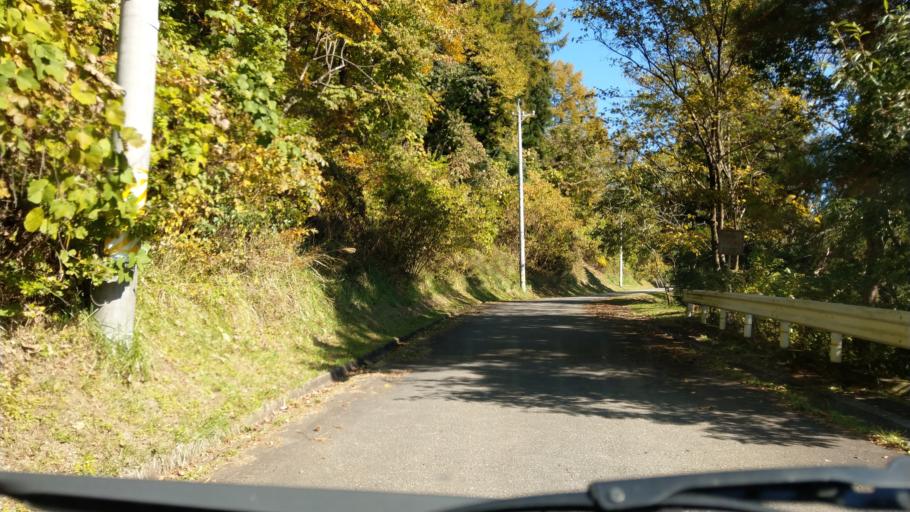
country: JP
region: Nagano
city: Komoro
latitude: 36.3650
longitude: 138.4460
